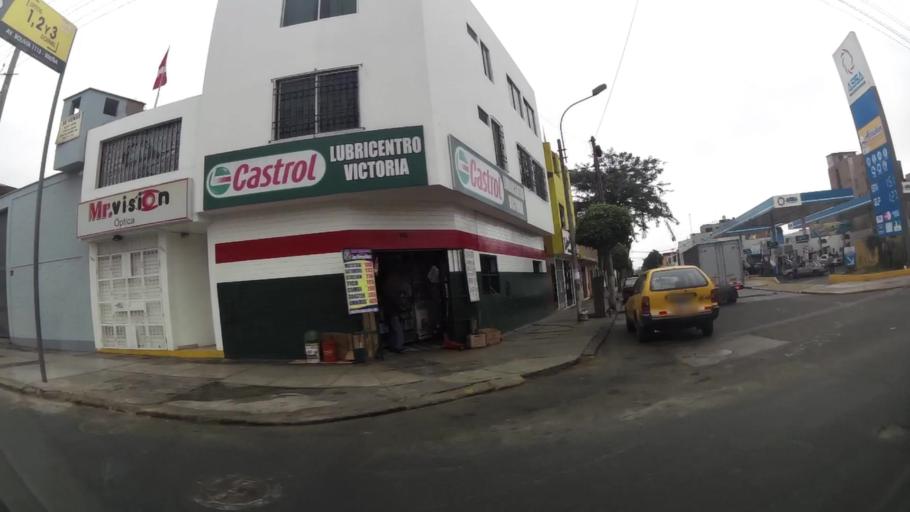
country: PE
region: Lima
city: Lima
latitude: -12.0566
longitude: -77.0542
